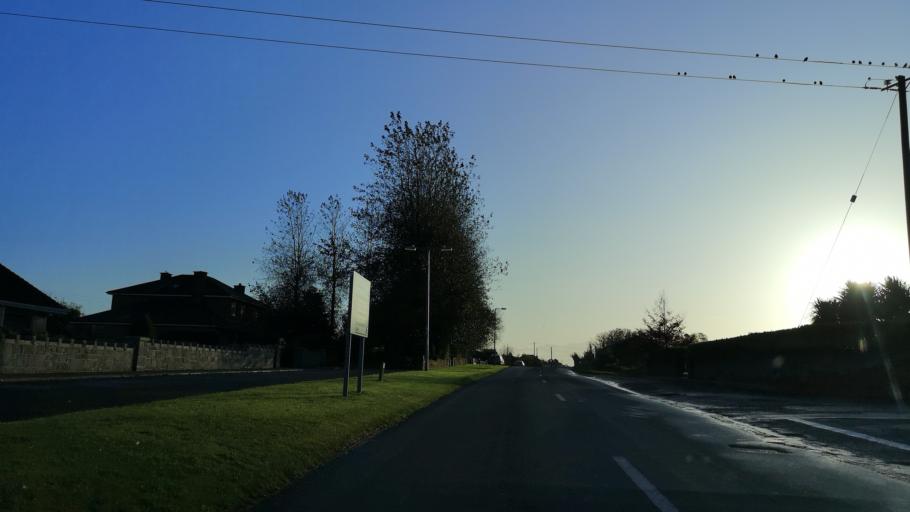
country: IE
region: Connaught
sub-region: Roscommon
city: Castlerea
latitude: 53.7579
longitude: -8.5161
